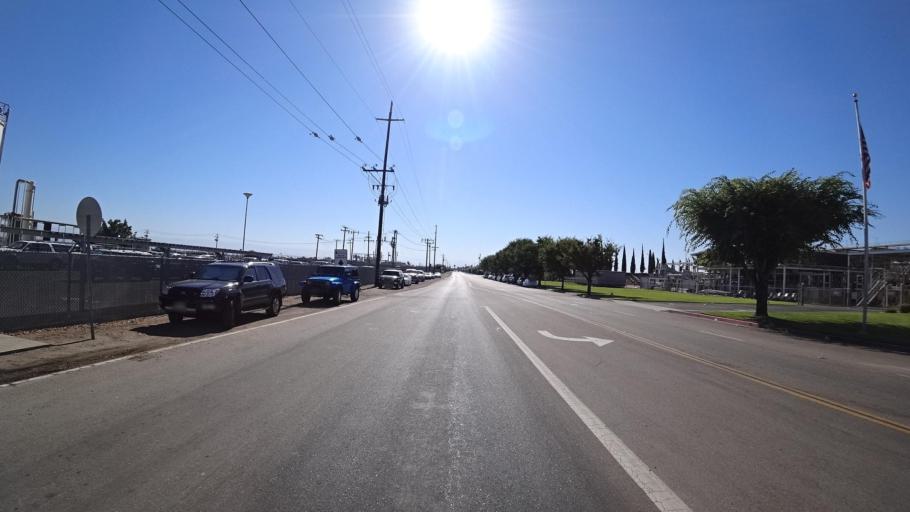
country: US
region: California
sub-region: Fresno County
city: Sunnyside
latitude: 36.7575
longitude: -119.6982
